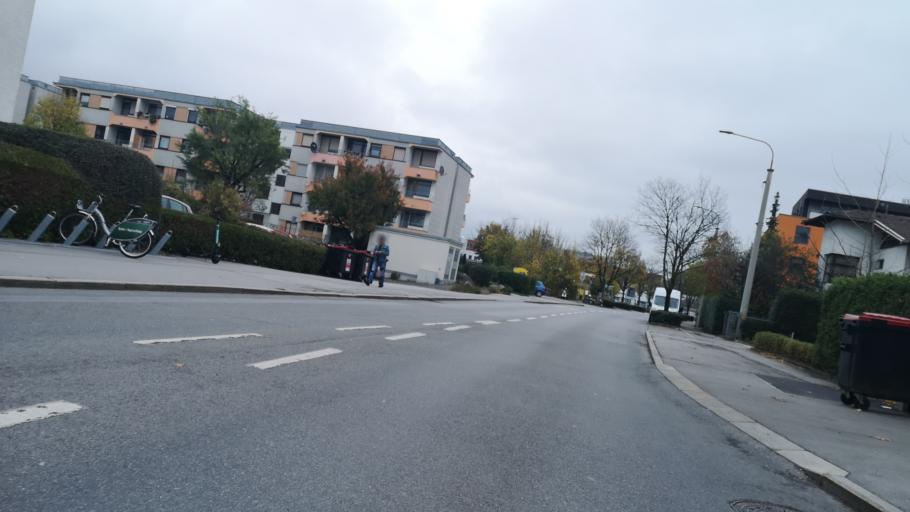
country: AT
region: Tyrol
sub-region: Politischer Bezirk Innsbruck Land
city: Natters
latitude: 47.2580
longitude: 11.3702
